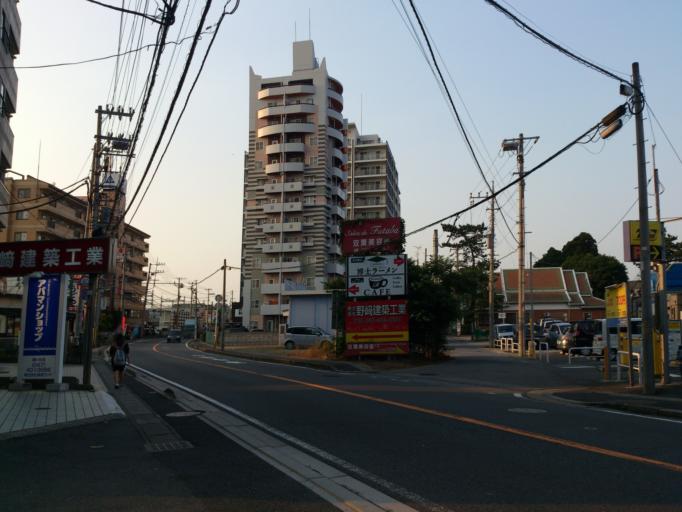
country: JP
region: Chiba
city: Funabashi
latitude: 35.7639
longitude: 139.9980
